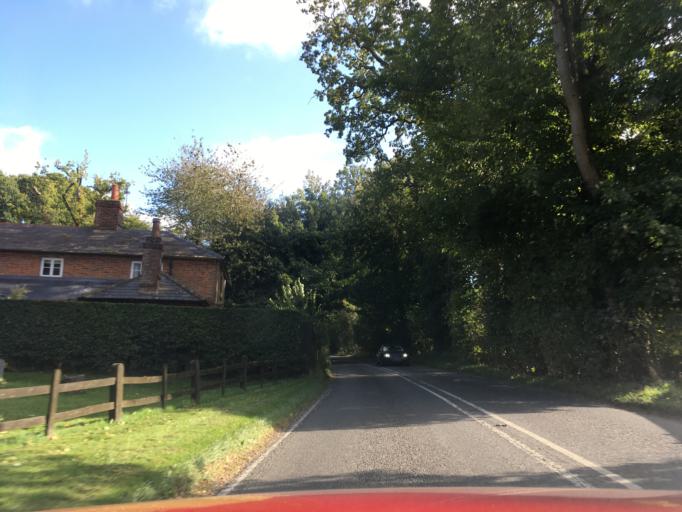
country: GB
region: England
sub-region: Hampshire
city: Old Basing
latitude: 51.2092
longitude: -1.0517
